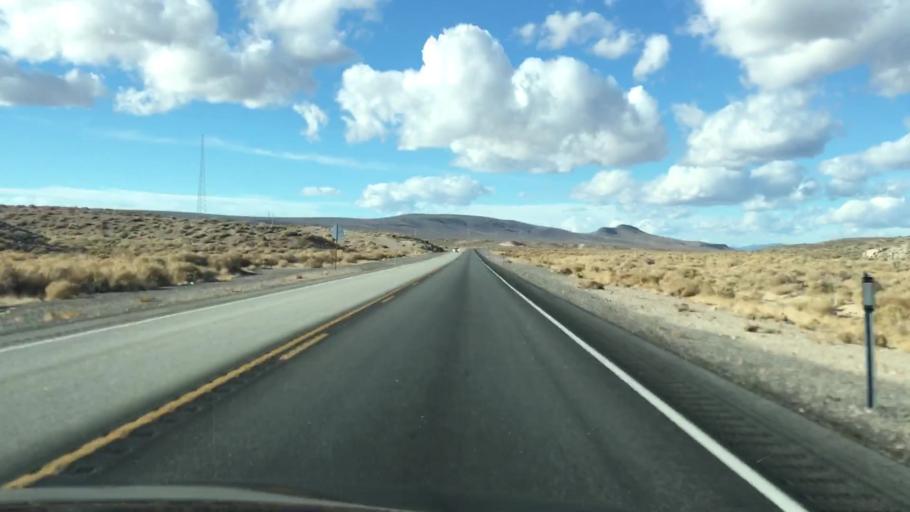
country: US
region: Nevada
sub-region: Nye County
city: Beatty
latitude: 37.0367
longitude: -116.7623
